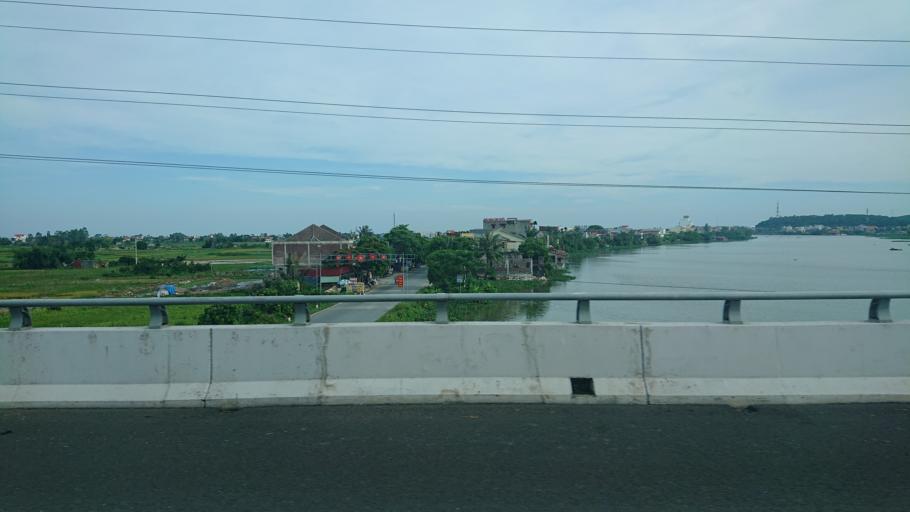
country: VN
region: Hai Phong
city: Nui Doi
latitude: 20.7653
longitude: 106.6764
